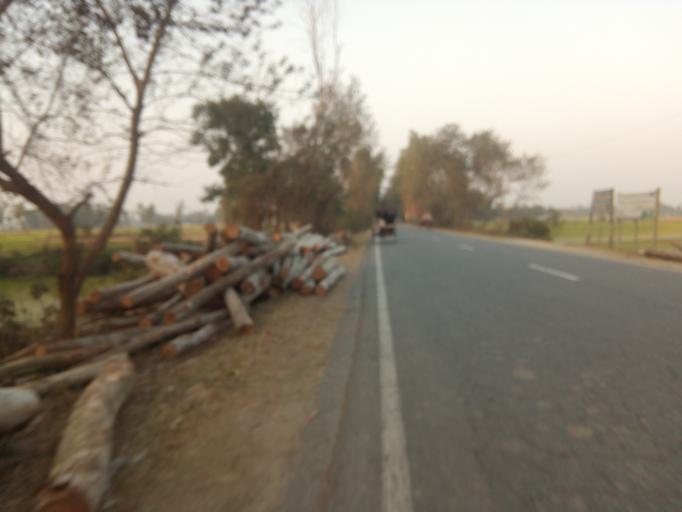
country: BD
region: Rajshahi
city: Bogra
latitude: 24.6288
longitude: 89.2446
